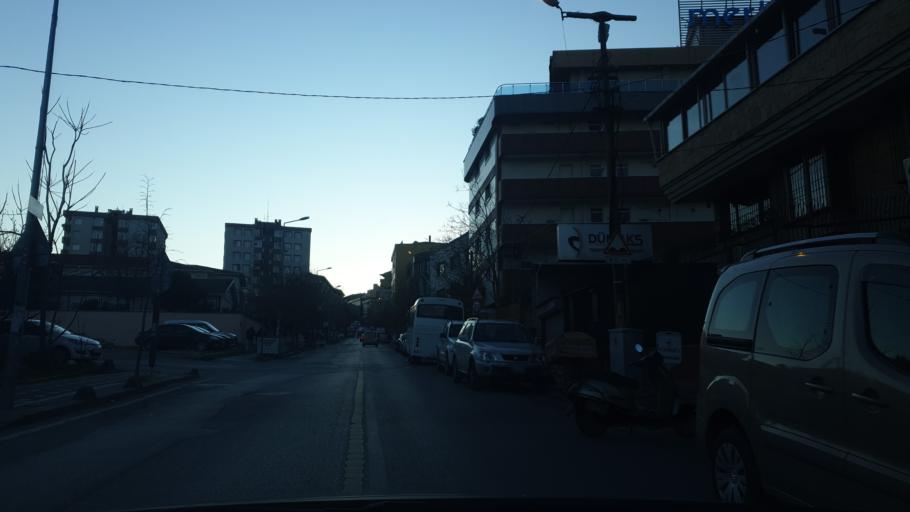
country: TR
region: Istanbul
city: Mahmutbey
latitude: 41.0067
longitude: 28.8062
